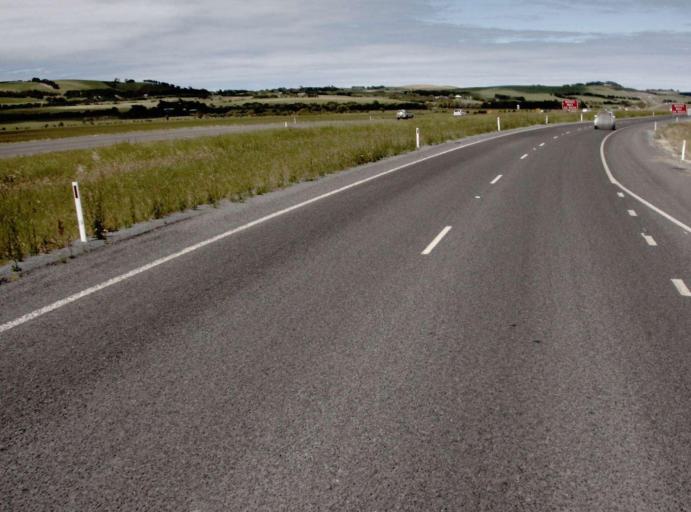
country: AU
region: Victoria
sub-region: Bass Coast
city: North Wonthaggi
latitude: -38.5014
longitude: 145.4603
